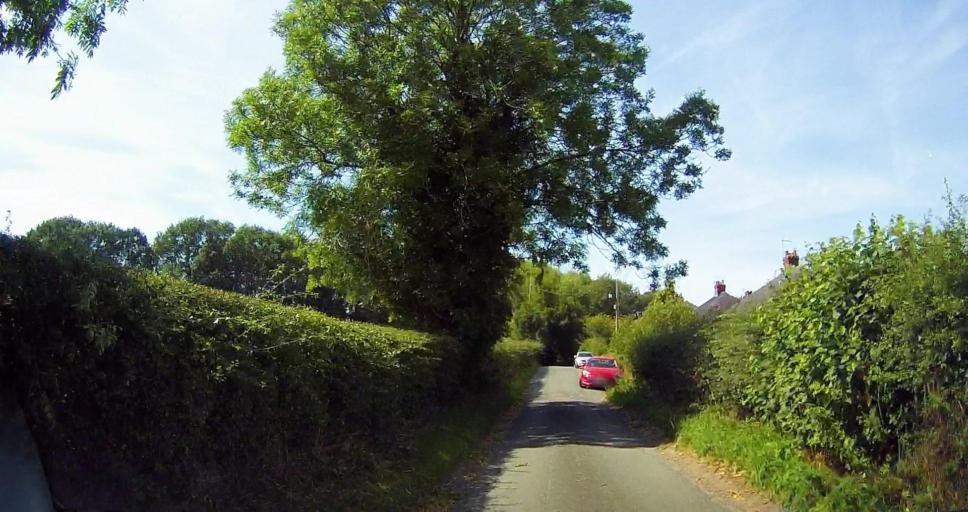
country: GB
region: England
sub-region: Shropshire
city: Market Drayton
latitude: 52.9801
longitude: -2.5151
